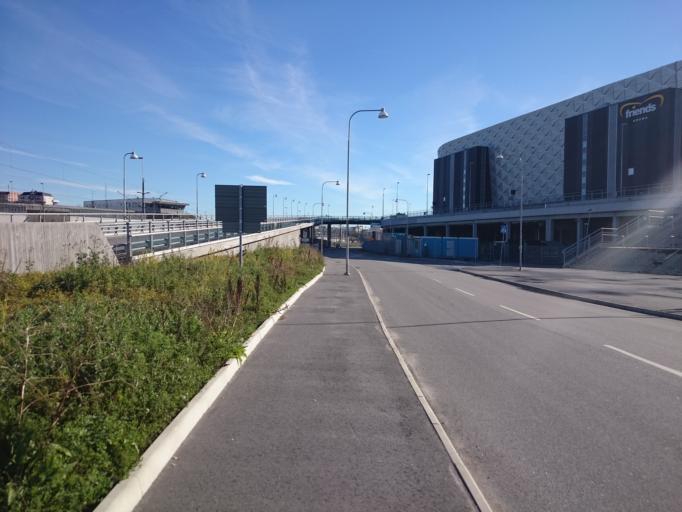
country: SE
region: Stockholm
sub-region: Solna Kommun
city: Solna
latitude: 59.3738
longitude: 17.9971
